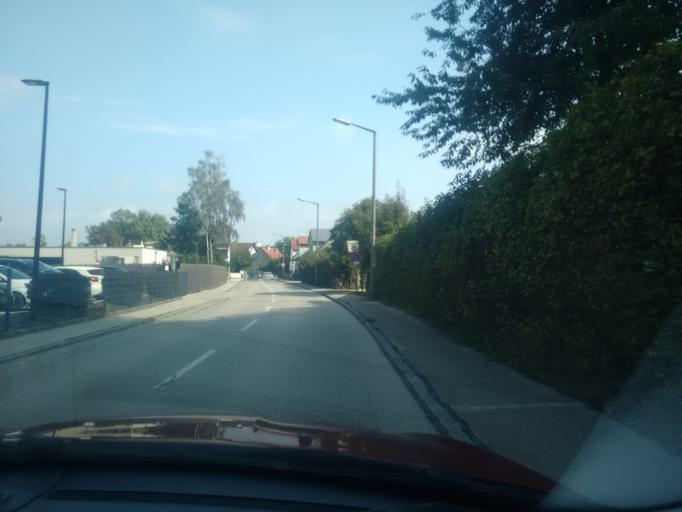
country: AT
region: Upper Austria
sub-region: Wels-Land
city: Thalheim bei Wels
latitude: 48.1485
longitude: 14.0208
